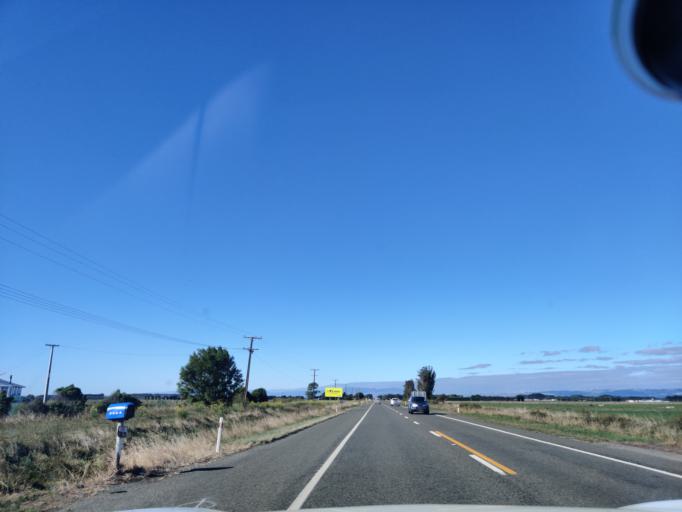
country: NZ
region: Manawatu-Wanganui
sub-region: Palmerston North City
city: Palmerston North
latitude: -40.4100
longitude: 175.4841
